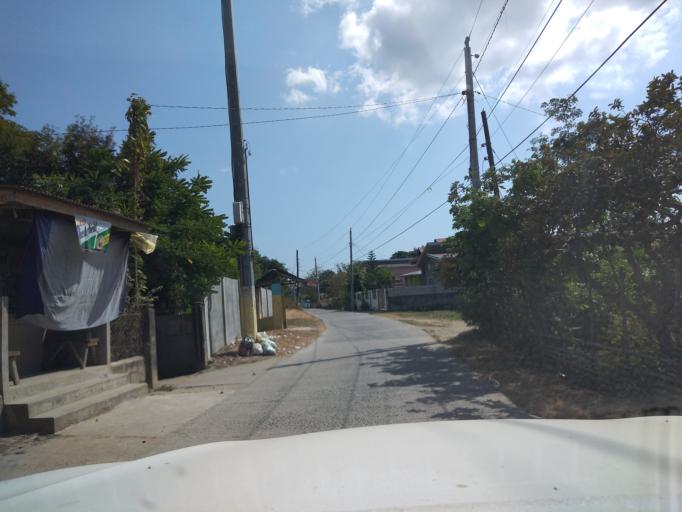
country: PH
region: Central Luzon
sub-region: Province of Pampanga
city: Candaba
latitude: 15.0857
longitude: 120.8121
